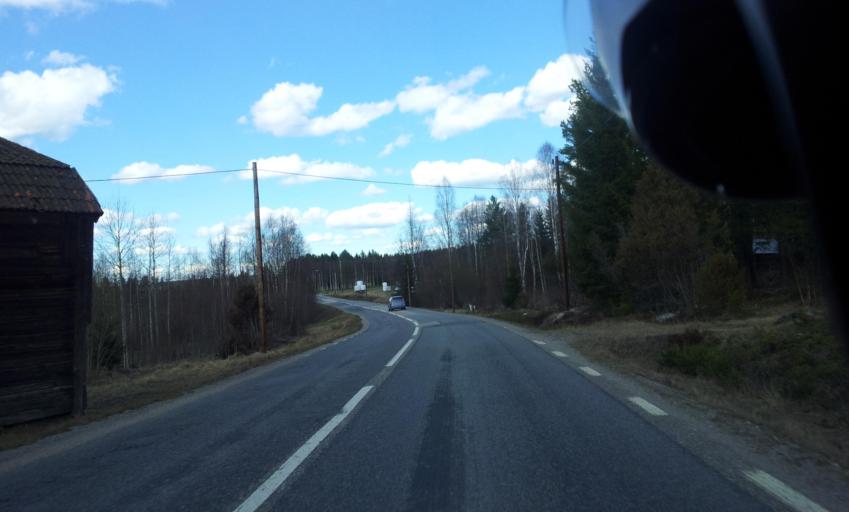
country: SE
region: Gaevleborg
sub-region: Ovanakers Kommun
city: Edsbyn
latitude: 61.2976
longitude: 15.8907
